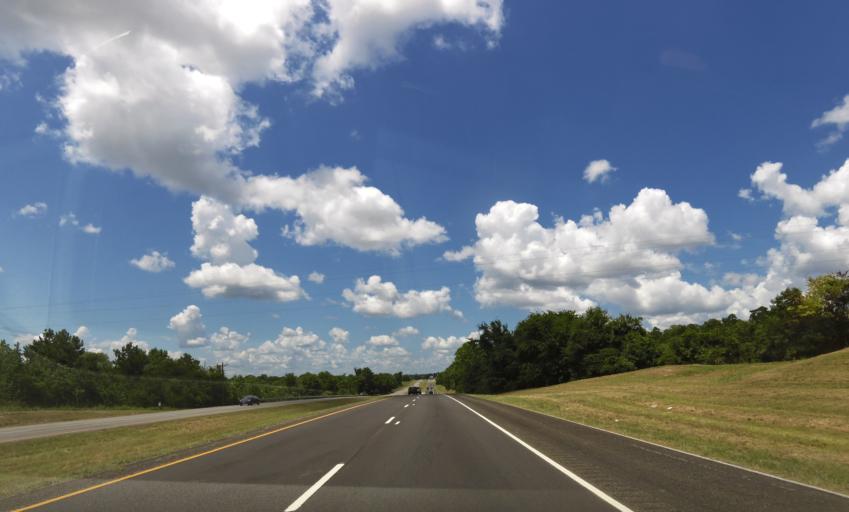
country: US
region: Texas
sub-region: Polk County
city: Livingston
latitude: 30.6359
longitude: -94.9461
